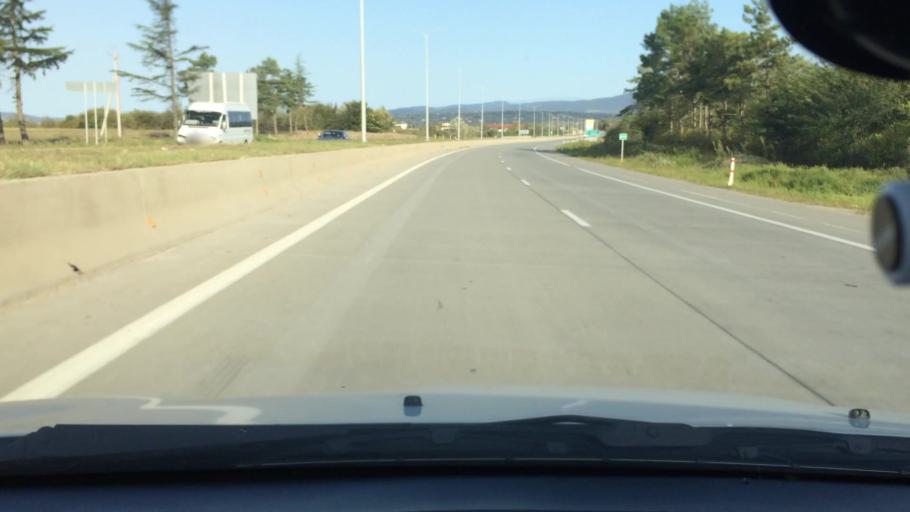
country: GE
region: Imereti
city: Zestap'oni
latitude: 42.1661
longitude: 42.9399
